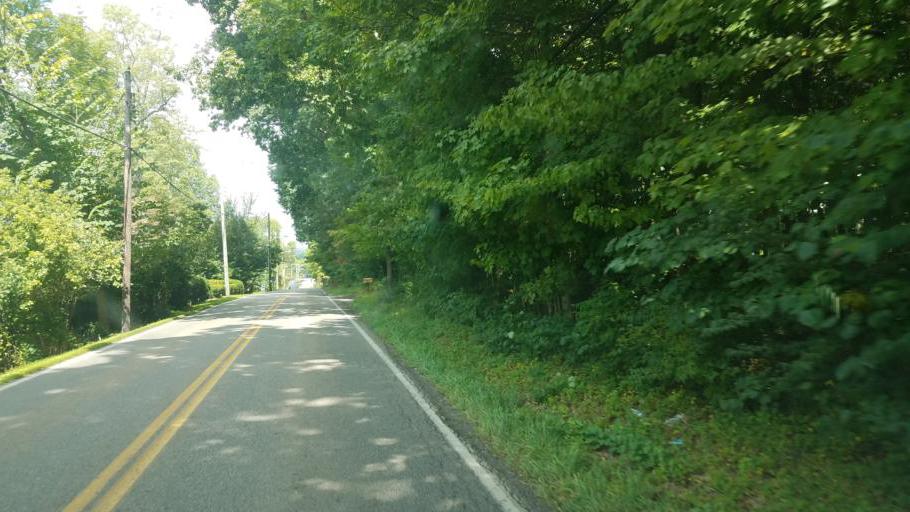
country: US
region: Ohio
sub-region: Knox County
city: Mount Vernon
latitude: 40.3907
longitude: -82.4640
